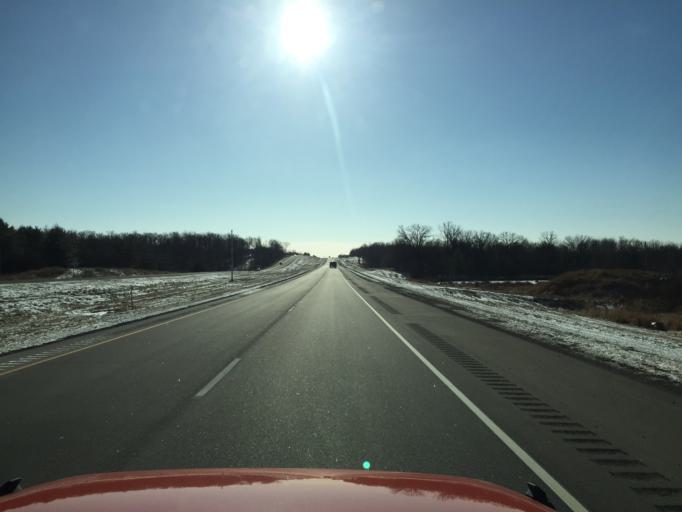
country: US
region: Minnesota
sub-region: Mille Lacs County
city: Milaca
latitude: 45.8174
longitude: -93.6554
